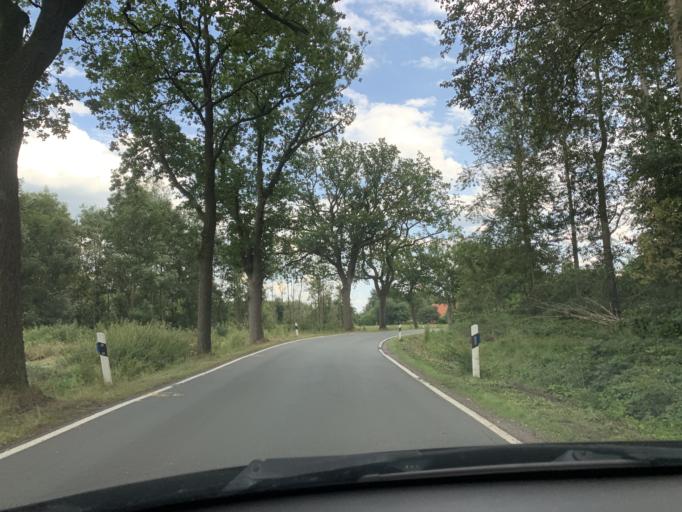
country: DE
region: Lower Saxony
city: Westerstede
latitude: 53.2412
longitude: 7.8689
